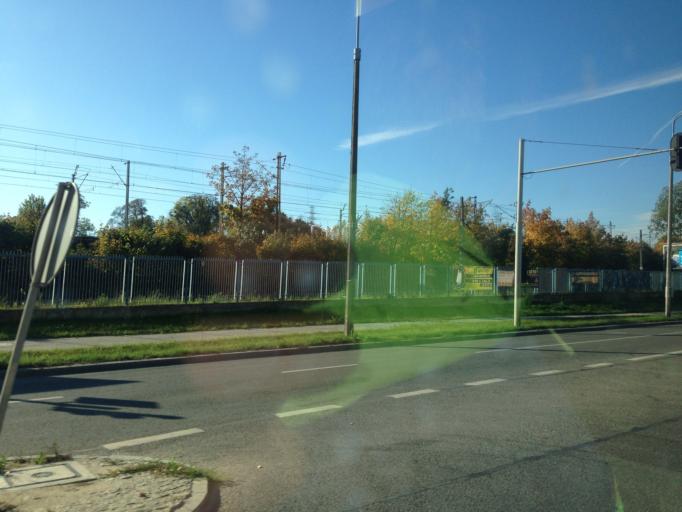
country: PL
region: Pomeranian Voivodeship
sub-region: Gdansk
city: Gdansk
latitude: 54.3722
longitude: 18.6332
